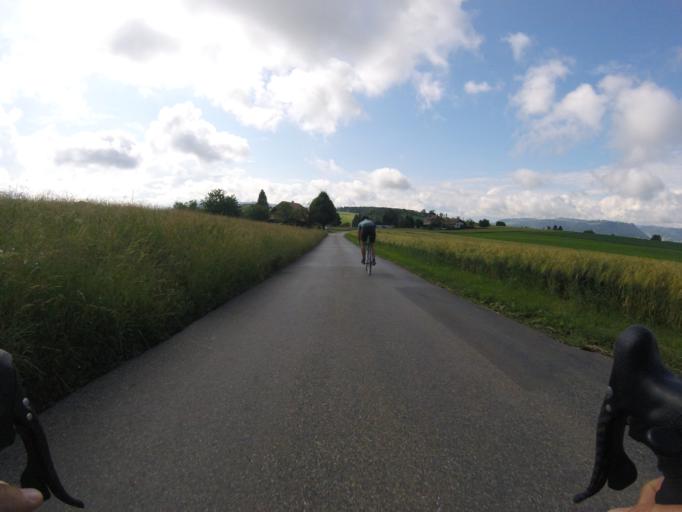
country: CH
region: Bern
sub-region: Bern-Mittelland District
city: Worb
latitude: 46.9330
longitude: 7.5453
